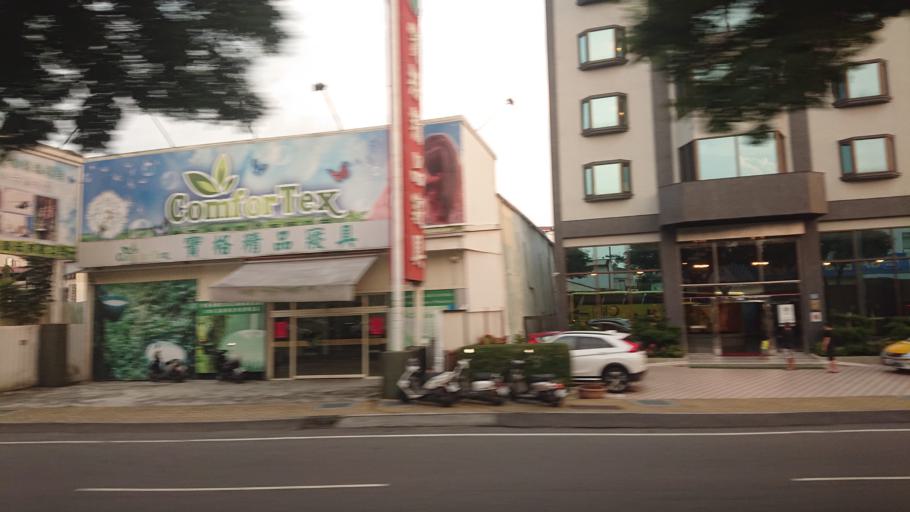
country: TW
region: Taiwan
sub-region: Nantou
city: Puli
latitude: 23.9732
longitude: 120.9642
